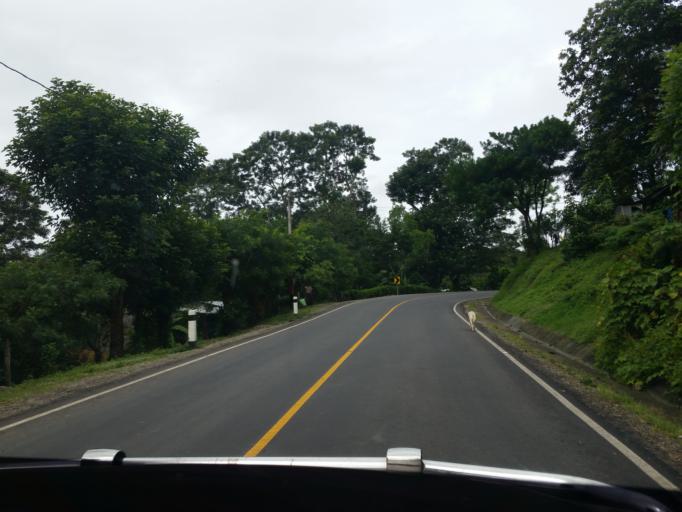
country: NI
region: Jinotega
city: Jinotega
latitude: 13.1495
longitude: -85.9574
